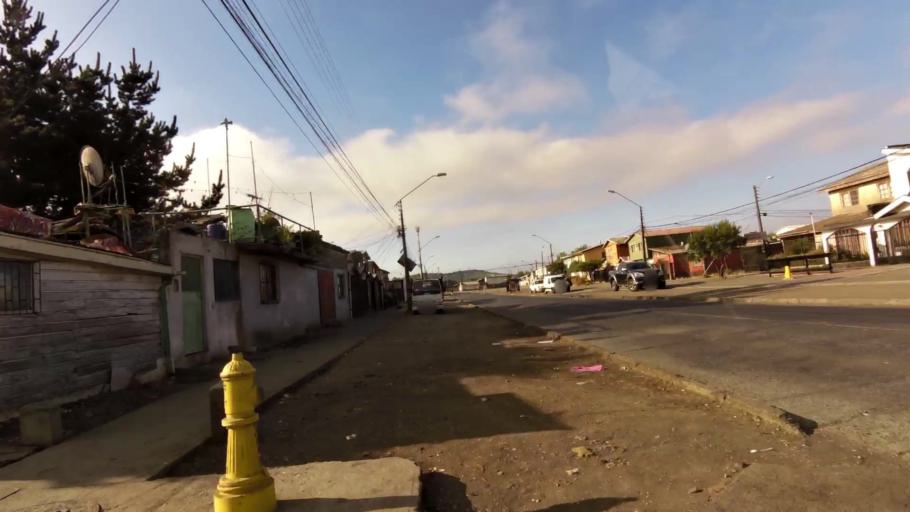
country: CL
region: Biobio
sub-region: Provincia de Concepcion
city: Concepcion
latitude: -36.7886
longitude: -73.0944
